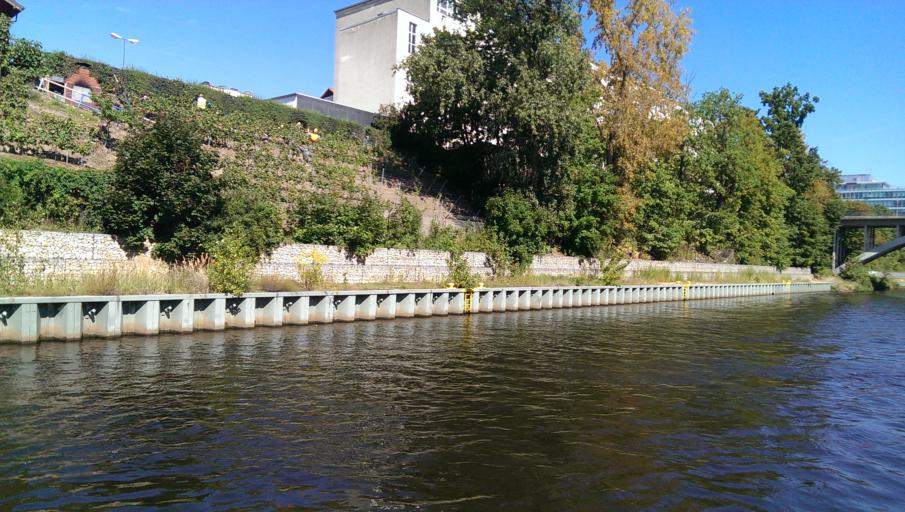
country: DE
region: Berlin
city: Tempelhof Bezirk
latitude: 52.4558
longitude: 13.3926
